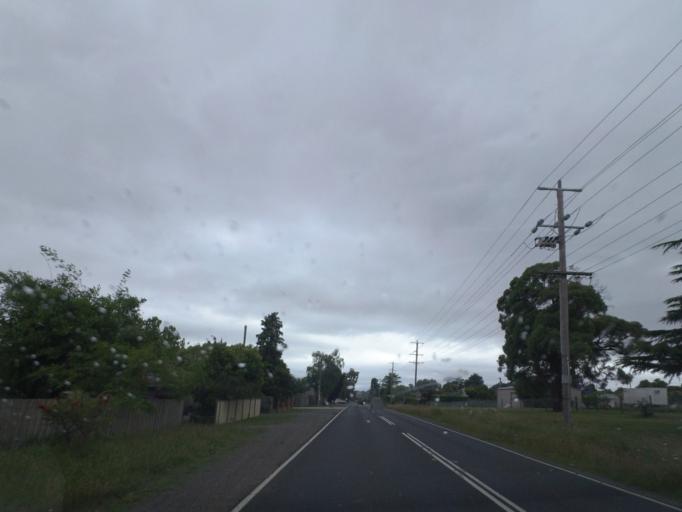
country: AU
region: Victoria
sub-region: Yarra Ranges
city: Mount Evelyn
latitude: -37.7820
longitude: 145.4260
